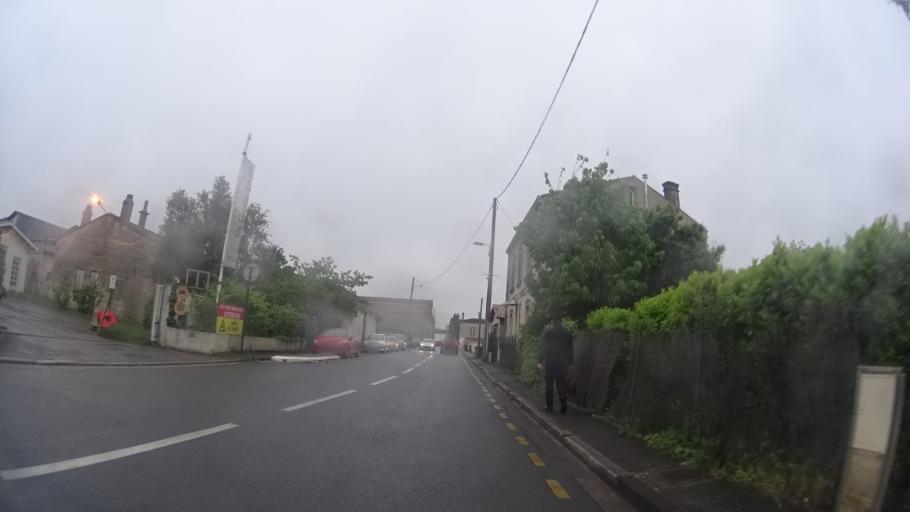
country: FR
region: Aquitaine
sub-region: Departement de la Gironde
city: Begles
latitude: 44.8328
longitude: -0.5432
